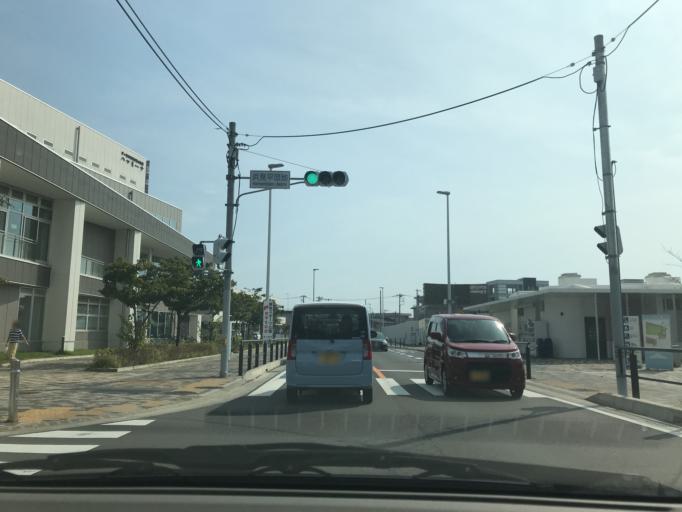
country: JP
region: Kanagawa
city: Chigasaki
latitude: 35.3240
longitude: 139.3884
